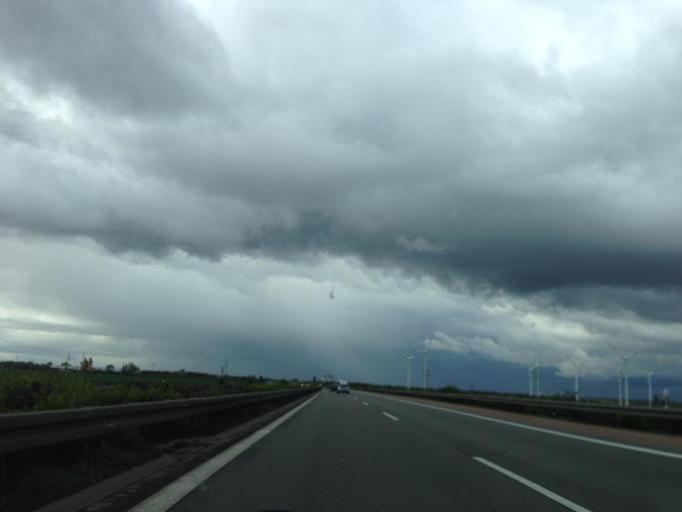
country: DE
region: Saxony-Anhalt
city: Konnern
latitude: 51.6668
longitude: 11.8045
